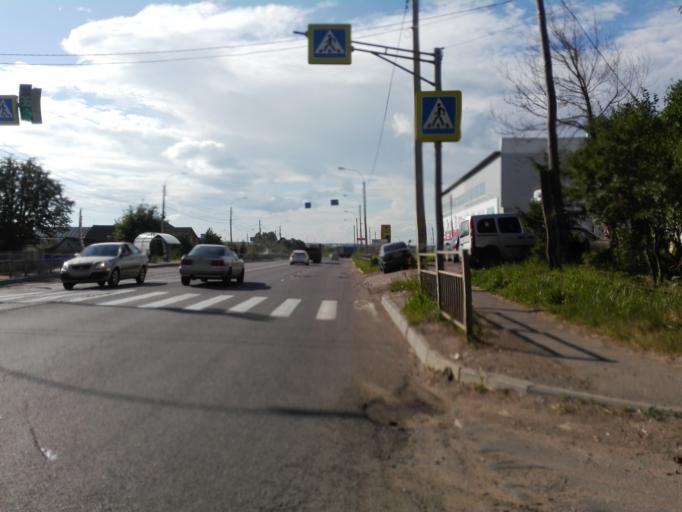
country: RU
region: Orjol
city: Orel
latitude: 52.9990
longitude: 36.1061
